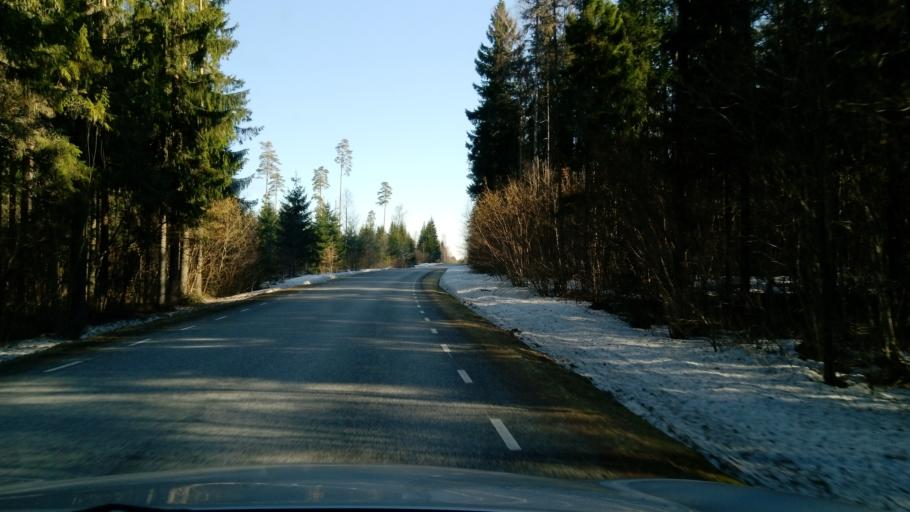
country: EE
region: Laeaene-Virumaa
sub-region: Tamsalu vald
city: Tamsalu
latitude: 59.2360
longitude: 26.1727
